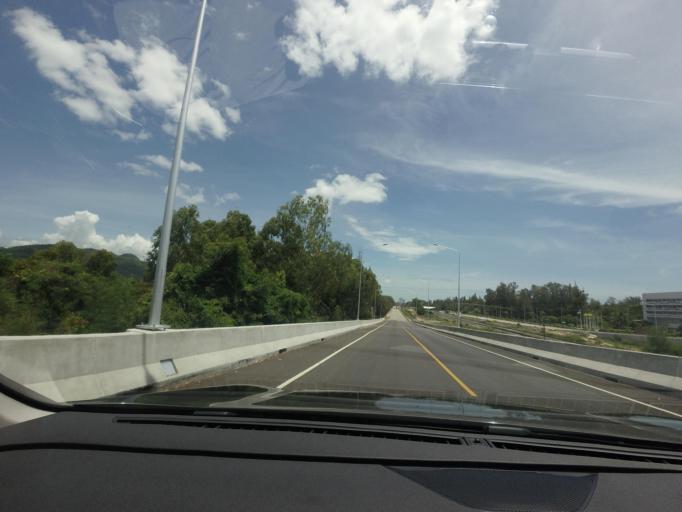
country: TH
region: Prachuap Khiri Khan
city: Hua Hin
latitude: 12.4943
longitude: 99.9722
